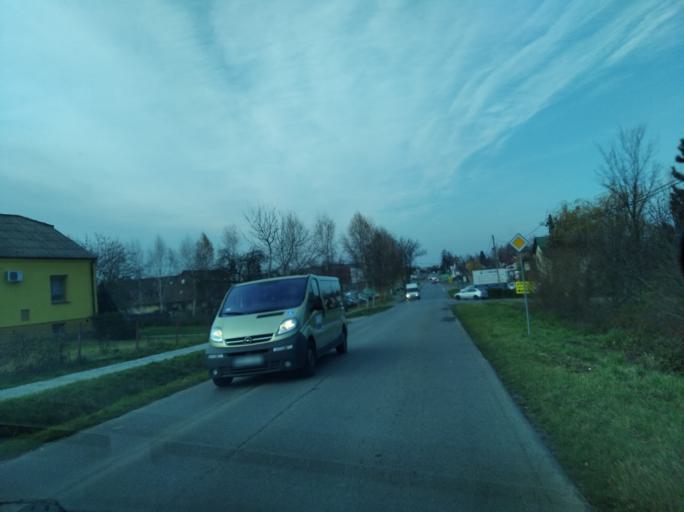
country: PL
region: Subcarpathian Voivodeship
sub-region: Powiat ropczycko-sedziszowski
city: Sedziszow Malopolski
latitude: 50.0623
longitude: 21.7330
